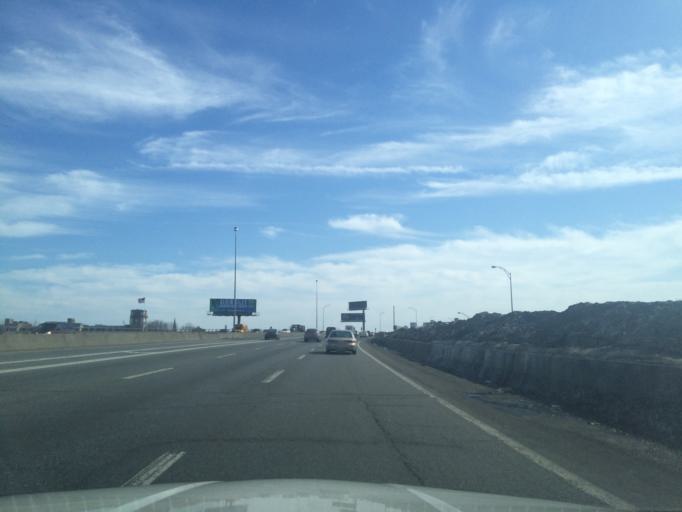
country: US
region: Massachusetts
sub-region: Middlesex County
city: Somerville
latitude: 42.3875
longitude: -71.0790
